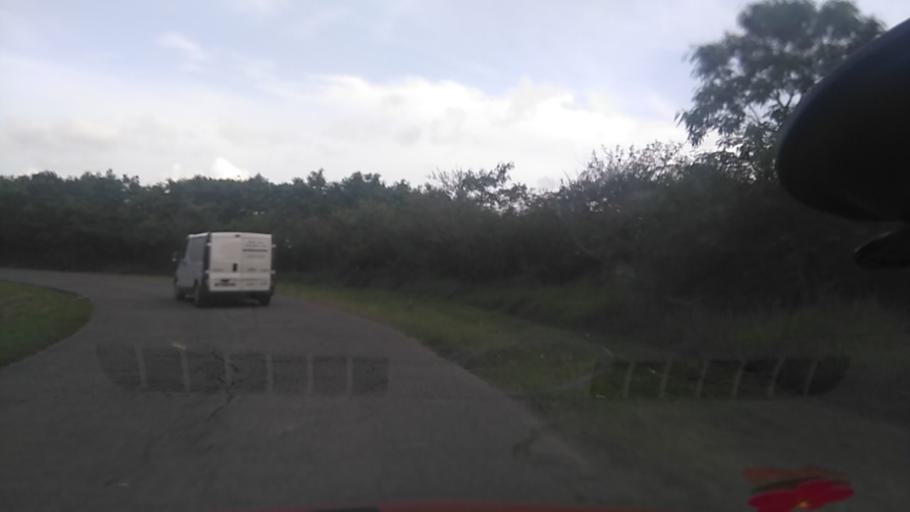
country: MQ
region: Martinique
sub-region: Martinique
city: Le Marin
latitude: 14.4674
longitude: -60.8640
